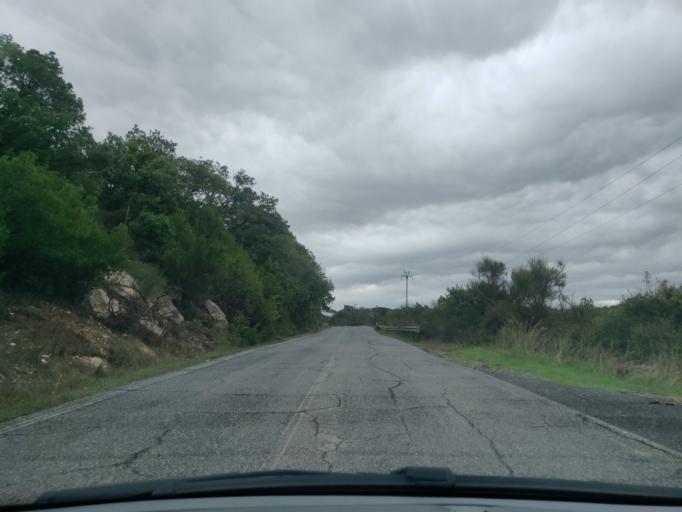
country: IT
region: Latium
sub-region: Citta metropolitana di Roma Capitale
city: Allumiere
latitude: 42.1255
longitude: 11.8607
